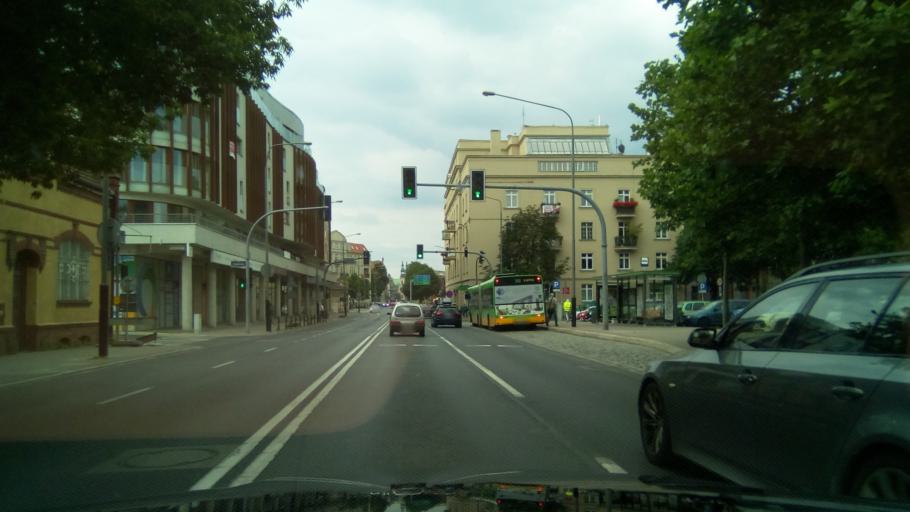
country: PL
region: Greater Poland Voivodeship
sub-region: Poznan
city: Poznan
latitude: 52.4134
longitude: 16.9390
